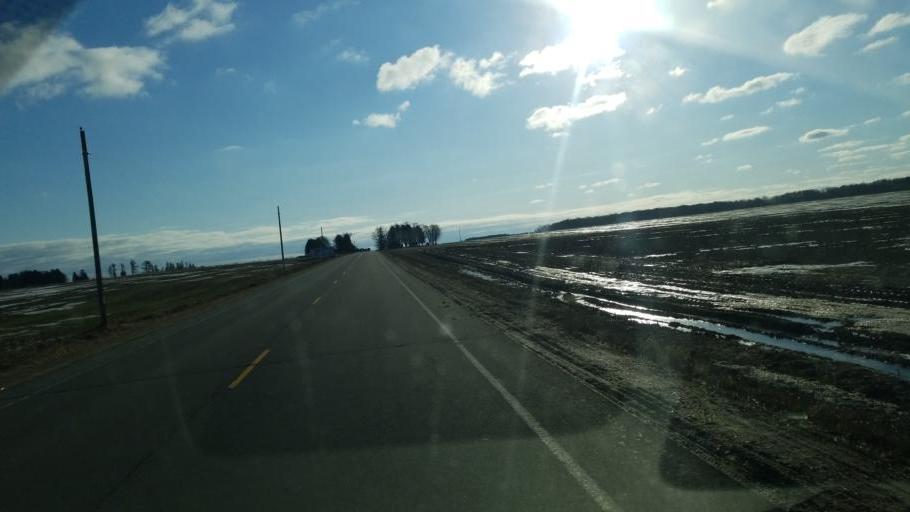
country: US
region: Wisconsin
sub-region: Clark County
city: Loyal
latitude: 44.6544
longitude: -90.4440
